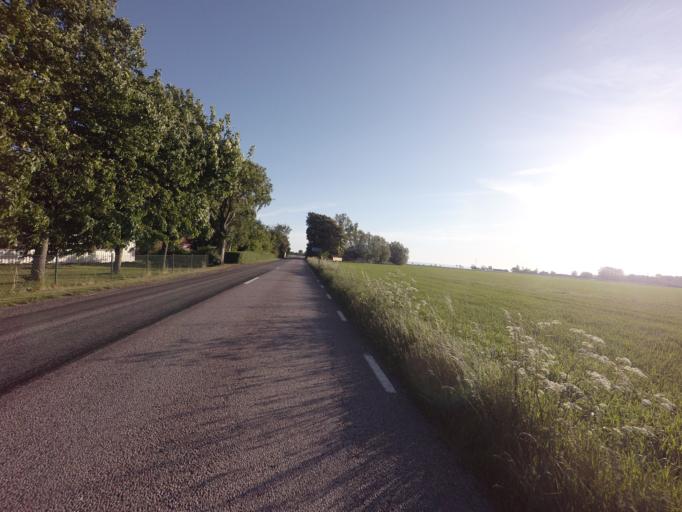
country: SE
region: Skane
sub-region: Hoganas Kommun
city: Hoganas
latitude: 56.2127
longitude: 12.6778
